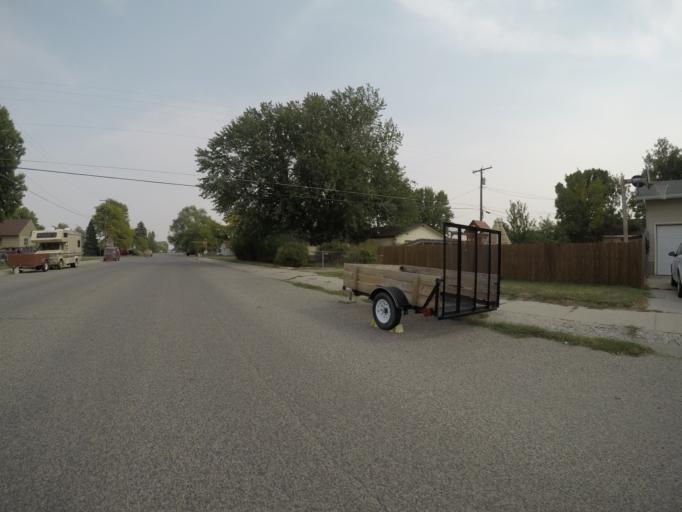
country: US
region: Montana
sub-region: Yellowstone County
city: Laurel
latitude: 45.6791
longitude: -108.7725
